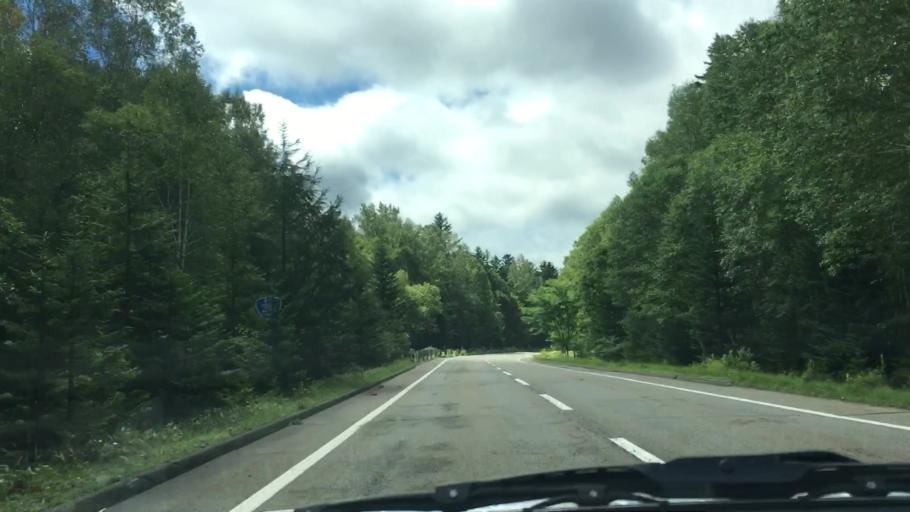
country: JP
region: Hokkaido
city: Kitami
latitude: 43.4154
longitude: 143.9737
